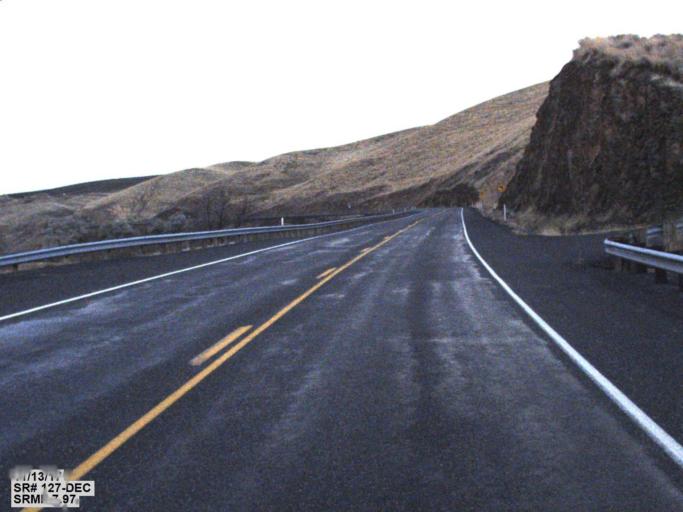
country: US
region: Washington
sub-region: Garfield County
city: Pomeroy
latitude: 46.6012
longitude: -117.7845
